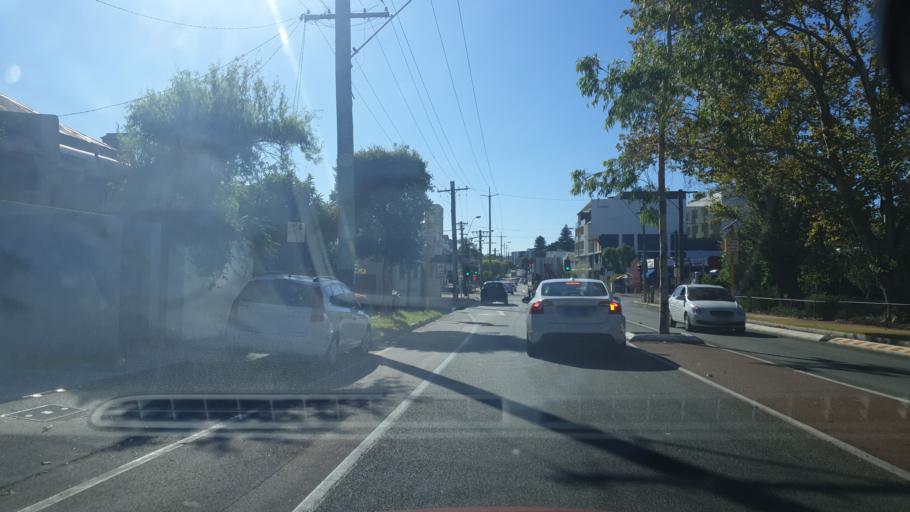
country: AU
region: Western Australia
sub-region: Vincent
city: Mount Lawley
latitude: -31.9422
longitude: 115.8663
